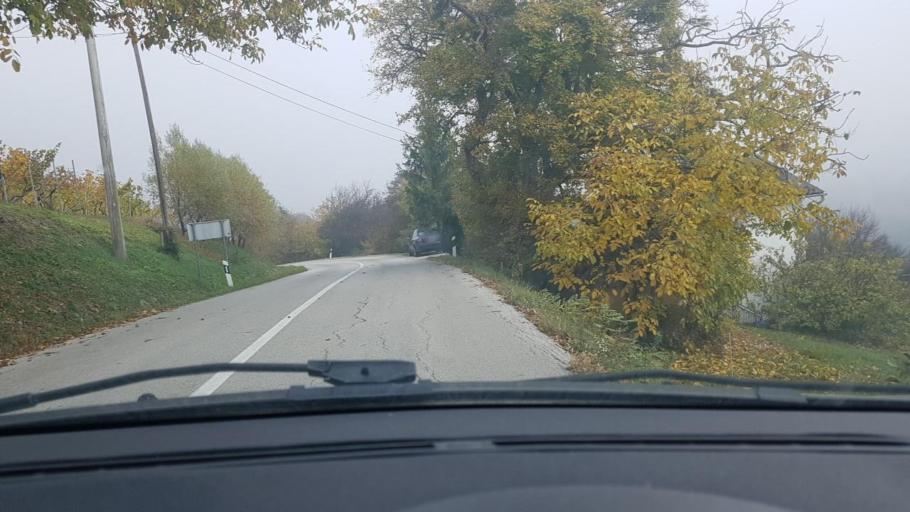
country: HR
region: Varazdinska
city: Ivanec
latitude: 46.1396
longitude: 16.1470
